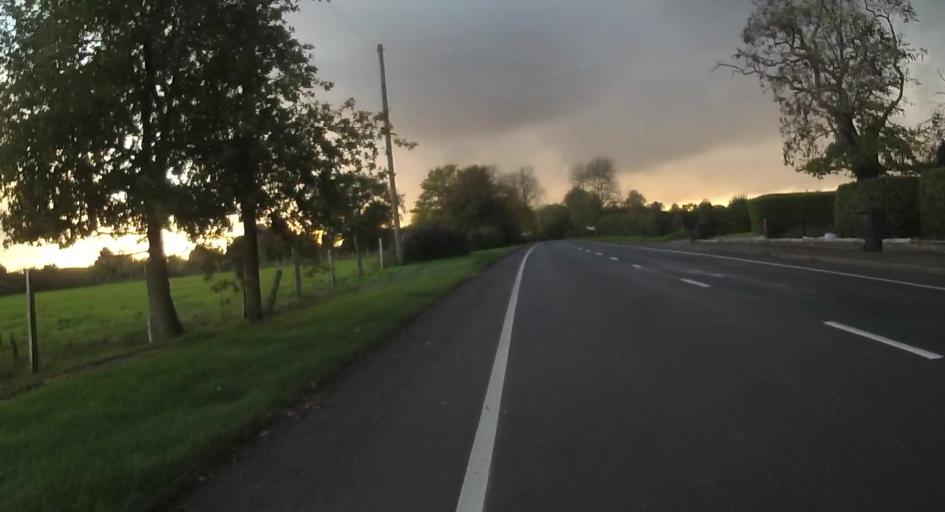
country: GB
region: England
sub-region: Hampshire
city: Kingsley
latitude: 51.1875
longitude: -0.8884
